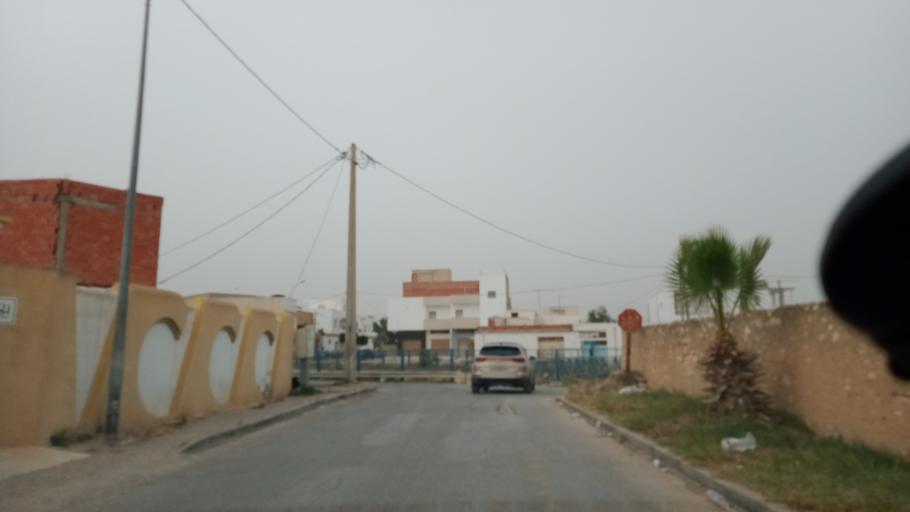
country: TN
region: Safaqis
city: Al Qarmadah
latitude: 34.7956
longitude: 10.7722
